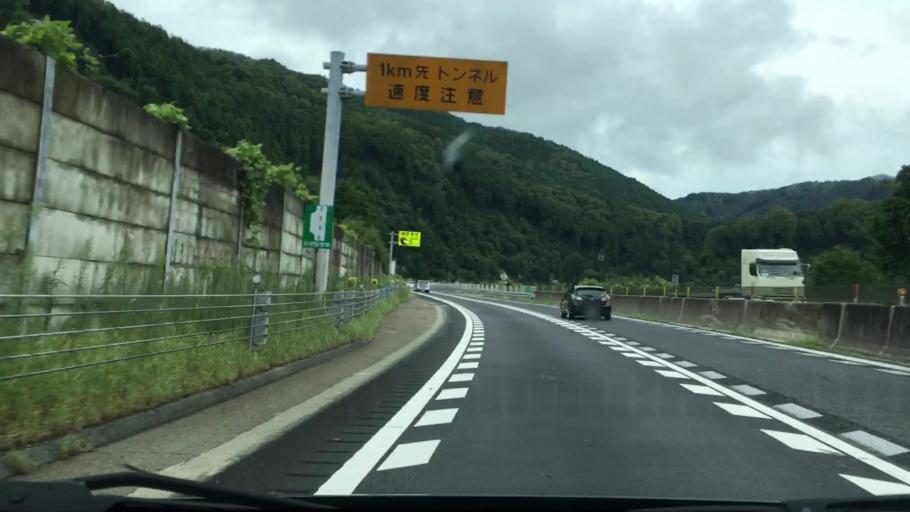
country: JP
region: Hyogo
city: Yamazakicho-nakabirose
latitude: 35.0452
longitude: 134.4507
